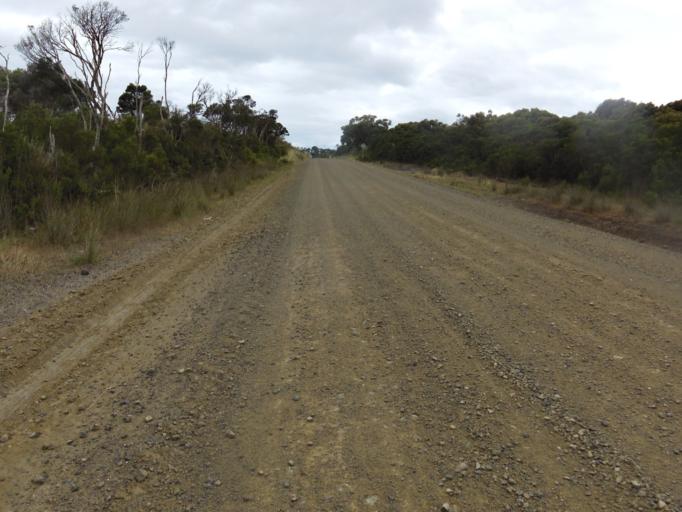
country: AU
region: Victoria
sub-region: Bass Coast
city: Cowes
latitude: -38.3861
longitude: 145.3200
